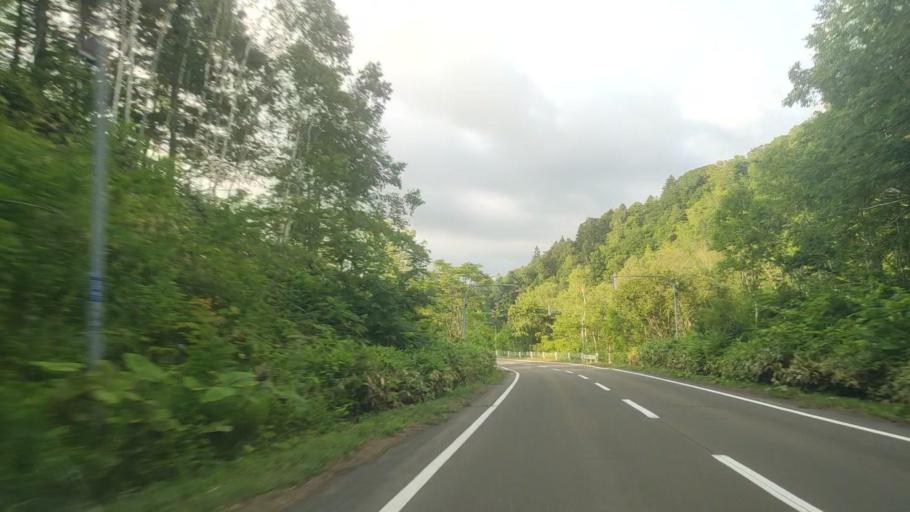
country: JP
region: Hokkaido
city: Bibai
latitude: 43.1372
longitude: 142.0966
